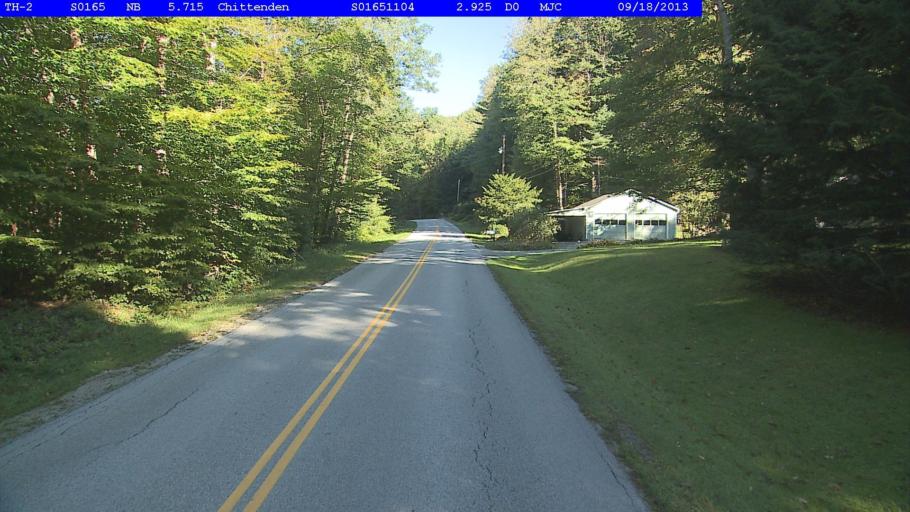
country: US
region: Vermont
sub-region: Rutland County
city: Rutland
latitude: 43.7177
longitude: -72.9628
